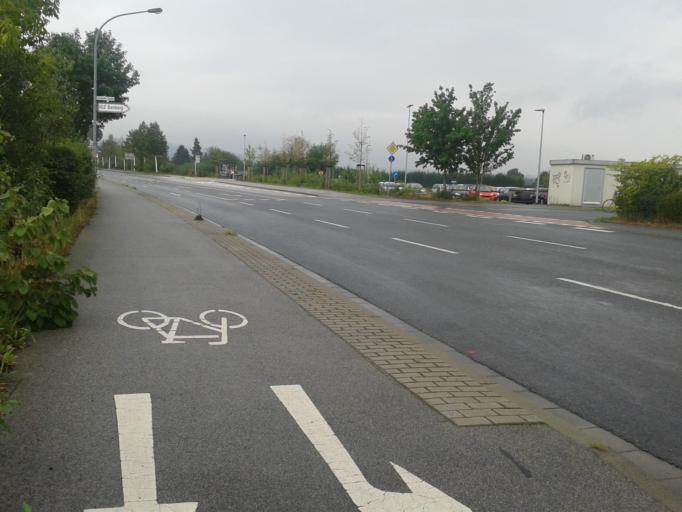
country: DE
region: Bavaria
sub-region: Upper Franconia
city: Bamberg
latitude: 49.9164
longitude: 10.8992
